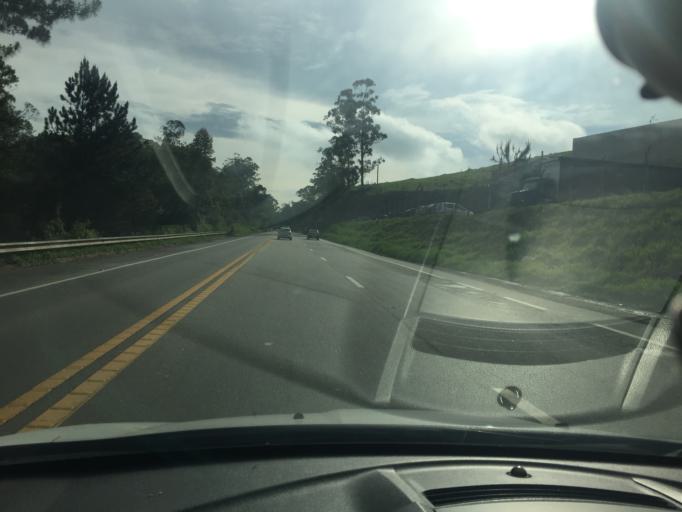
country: BR
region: Sao Paulo
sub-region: Campo Limpo Paulista
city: Campo Limpo Paulista
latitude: -23.1708
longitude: -46.7685
